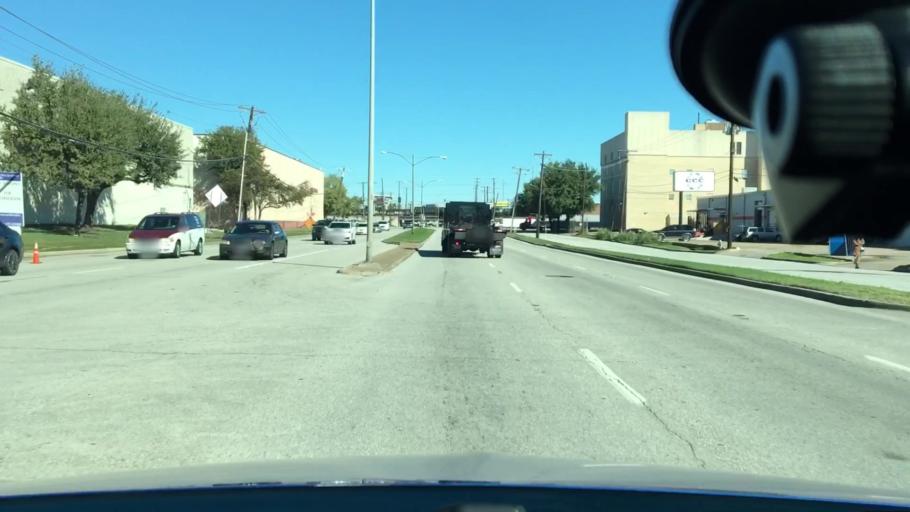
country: US
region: Texas
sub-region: Dallas County
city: Dallas
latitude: 32.8100
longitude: -96.8736
